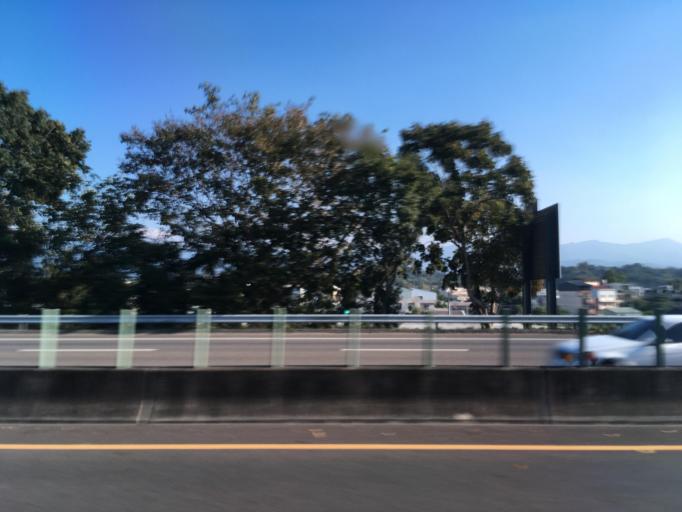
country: TW
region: Taiwan
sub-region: Chiayi
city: Jiayi Shi
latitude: 23.4360
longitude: 120.4763
